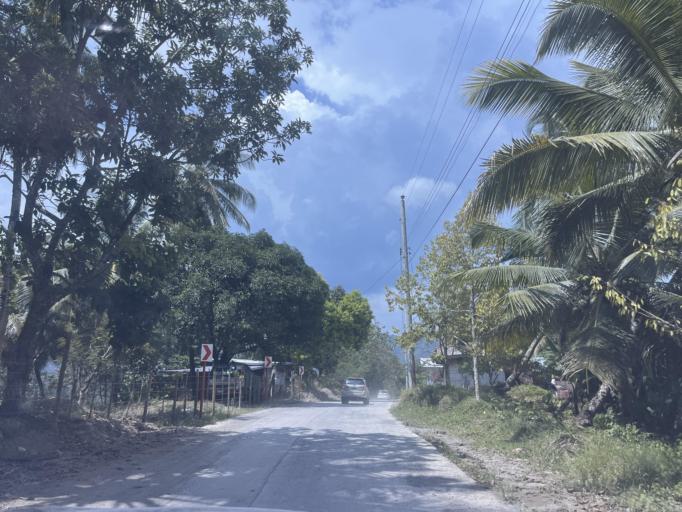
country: PH
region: Davao
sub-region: Province of Davao del Sur
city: Tamugan
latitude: 7.2842
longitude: 125.3376
